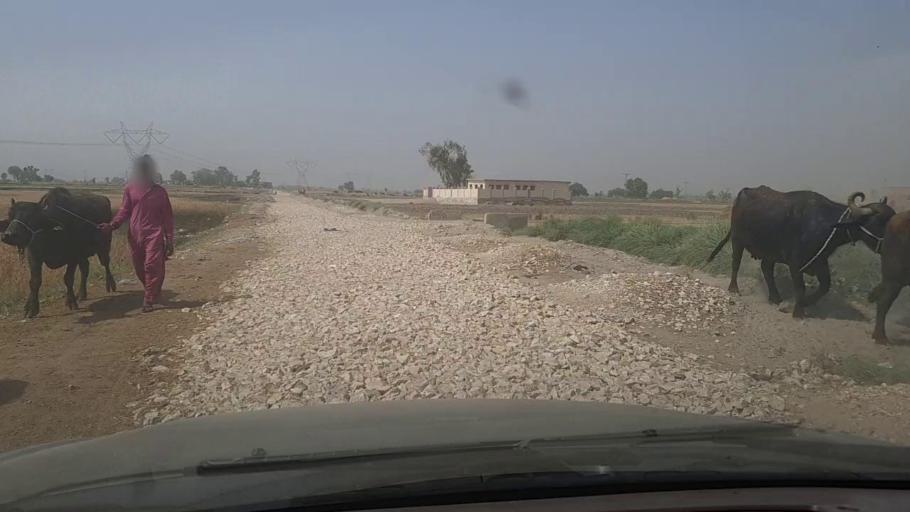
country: PK
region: Sindh
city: Madeji
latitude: 27.7935
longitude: 68.4862
